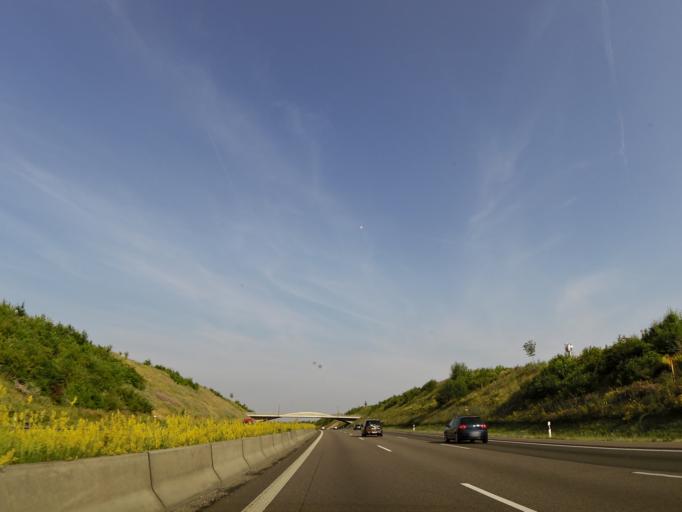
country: DE
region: Baden-Wuerttemberg
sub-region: Regierungsbezirk Stuttgart
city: Rutesheim
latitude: 48.7969
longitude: 8.9566
